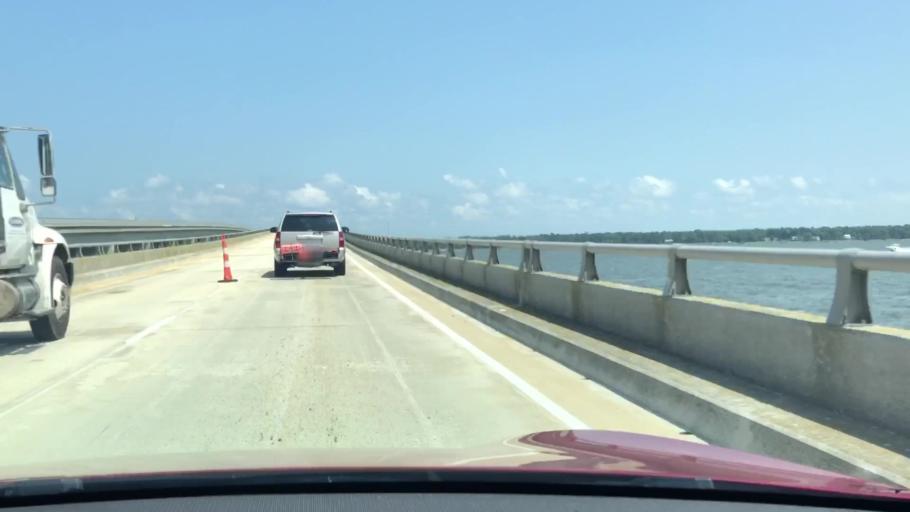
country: US
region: North Carolina
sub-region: Dare County
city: Southern Shores
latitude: 36.0881
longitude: -75.7600
